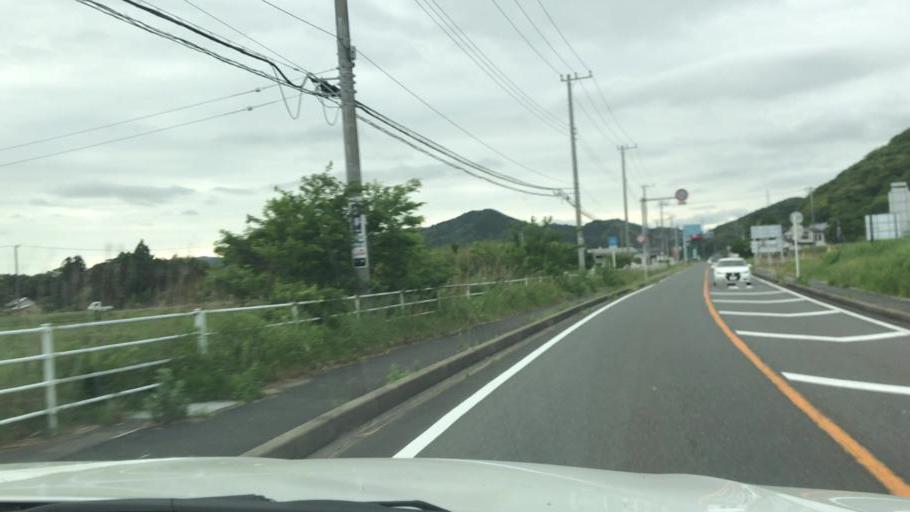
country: JP
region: Chiba
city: Kawaguchi
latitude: 35.1232
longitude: 140.0819
